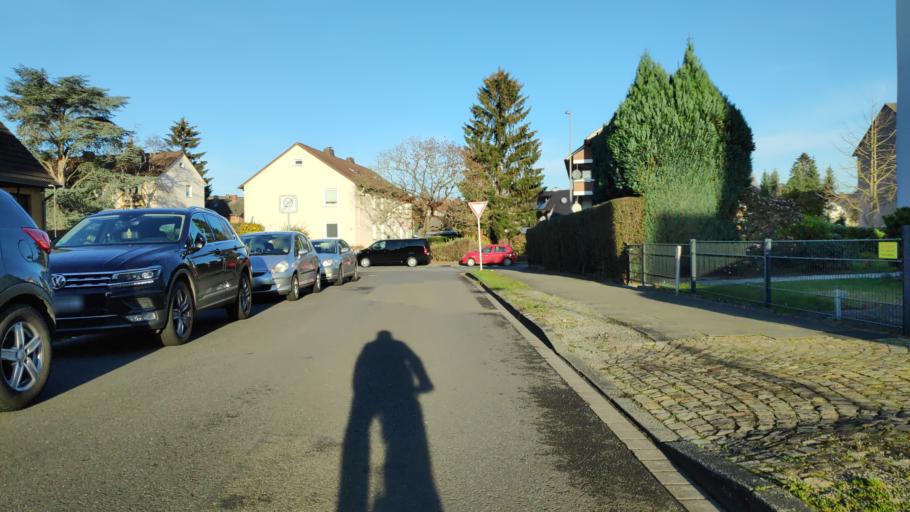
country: DE
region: North Rhine-Westphalia
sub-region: Regierungsbezirk Detmold
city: Minden
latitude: 52.2842
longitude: 8.8965
